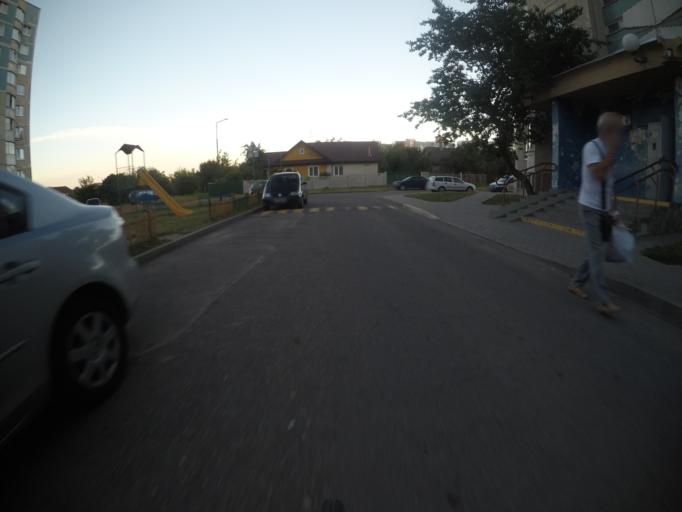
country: BY
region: Grodnenskaya
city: Hrodna
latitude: 53.7030
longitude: 23.8572
